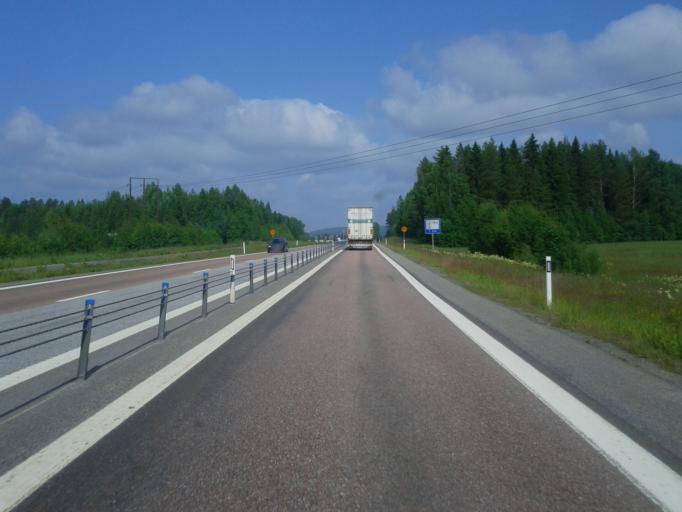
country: SE
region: Vaesterbotten
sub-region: Skelleftea Kommun
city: Skelleftea
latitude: 64.7226
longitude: 20.9838
